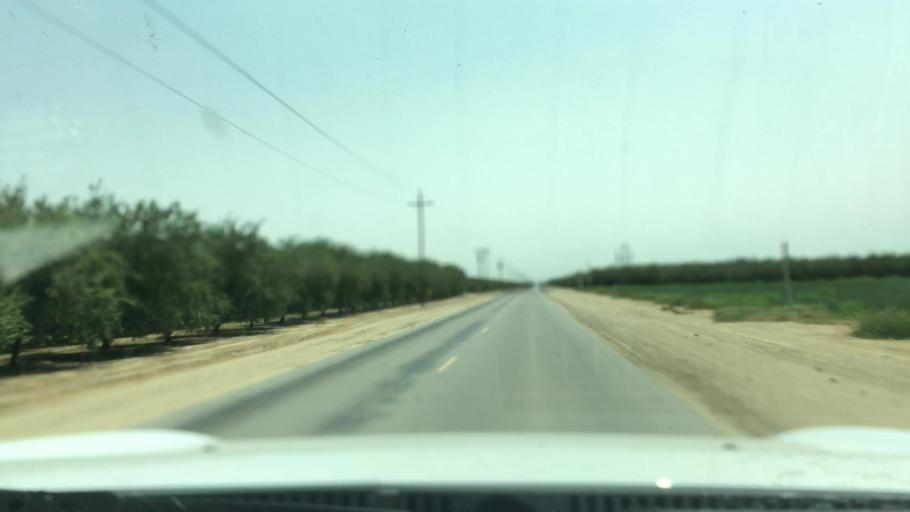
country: US
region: California
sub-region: Kern County
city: Wasco
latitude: 35.6469
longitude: -119.4375
